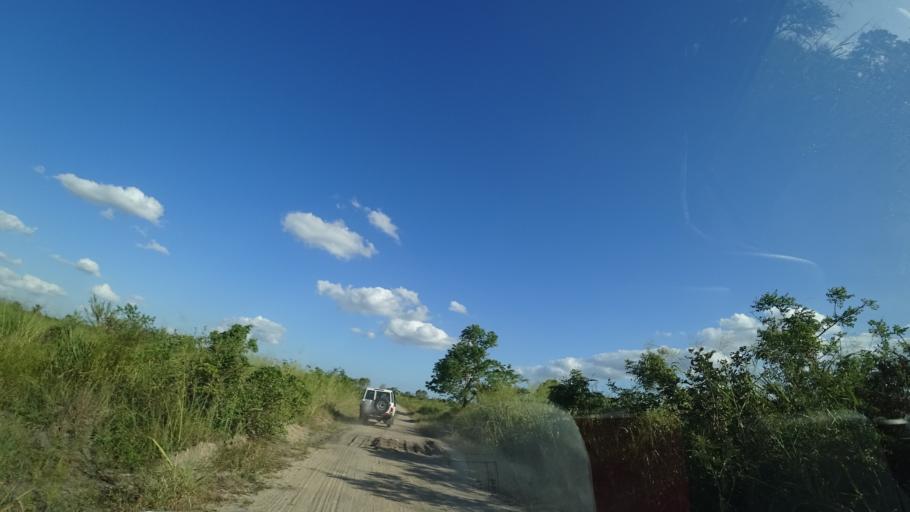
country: MZ
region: Sofala
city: Dondo
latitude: -19.3831
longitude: 34.5925
